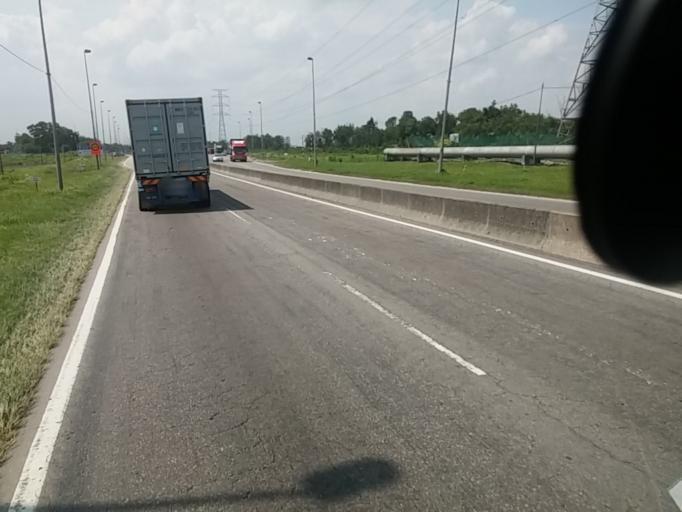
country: MY
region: Selangor
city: Klang
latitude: 2.9680
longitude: 101.3619
